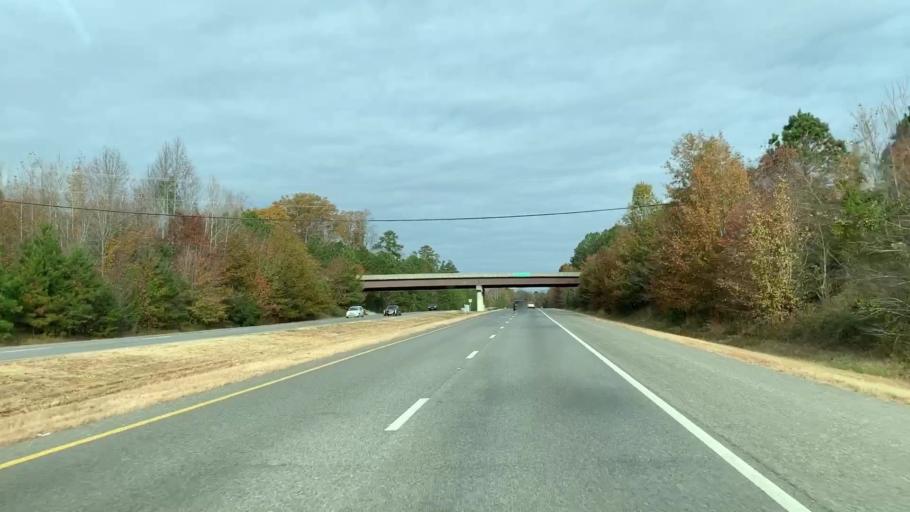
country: US
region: Virginia
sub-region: James City County
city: Williamsburg
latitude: 37.3095
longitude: -76.7465
